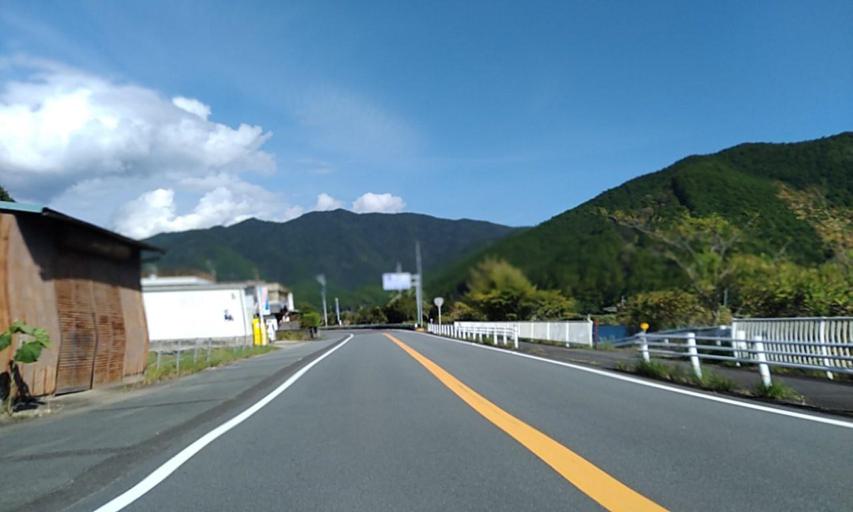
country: JP
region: Mie
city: Owase
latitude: 34.2146
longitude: 136.3445
